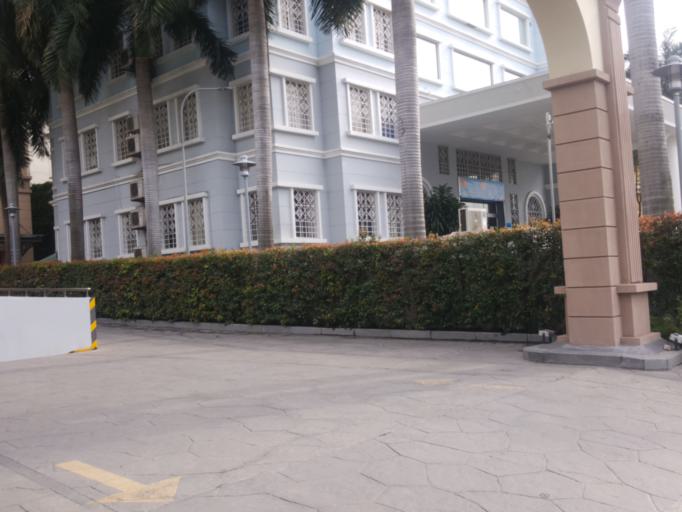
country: VN
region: Ho Chi Minh City
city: Quan Bon
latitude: 10.7662
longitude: 106.7027
